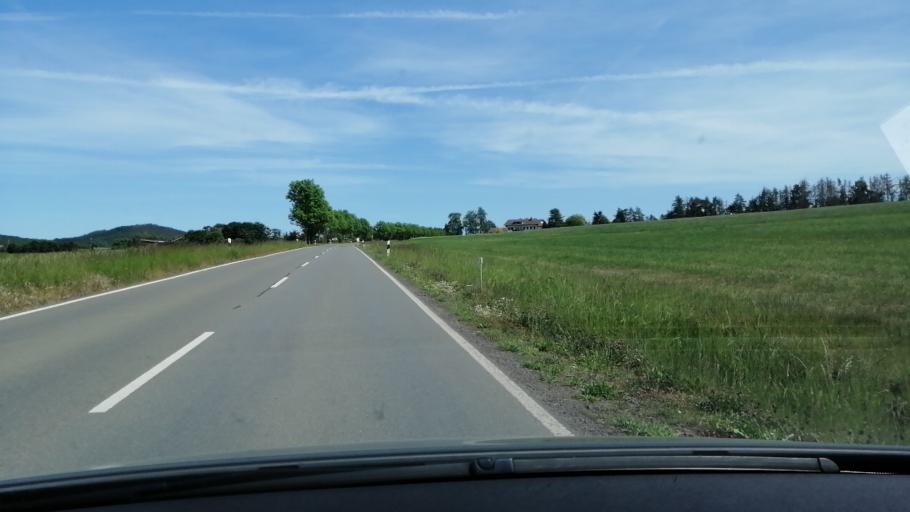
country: DE
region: Hesse
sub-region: Regierungsbezirk Kassel
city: Waldeck
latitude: 51.1800
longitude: 9.0318
